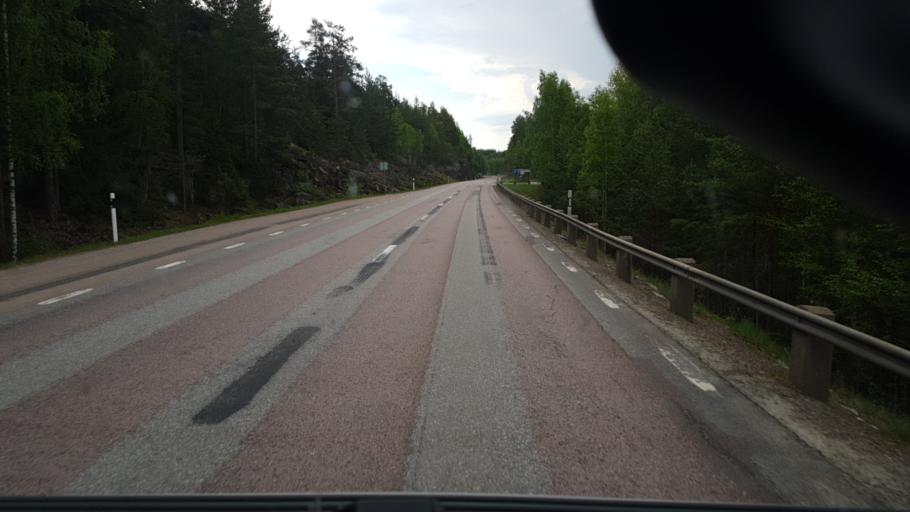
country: SE
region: Vaermland
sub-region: Arvika Kommun
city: Arvika
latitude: 59.5623
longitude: 12.7225
